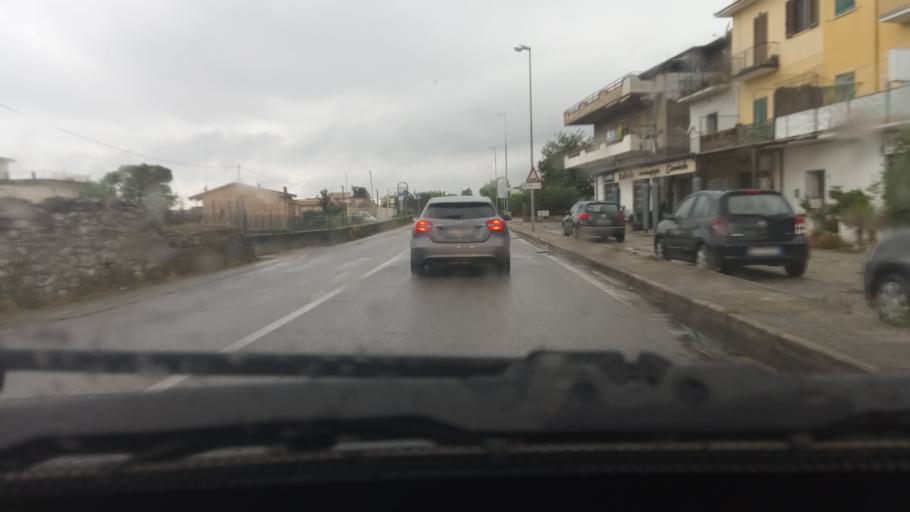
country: IT
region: Latium
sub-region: Provincia di Latina
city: Penitro
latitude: 41.2644
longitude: 13.6778
